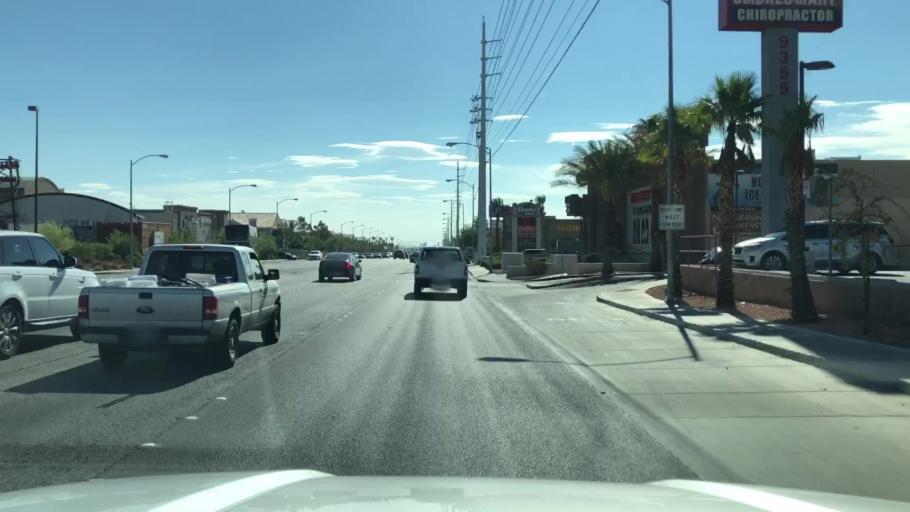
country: US
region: Nevada
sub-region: Clark County
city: Summerlin South
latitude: 36.1149
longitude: -115.2953
